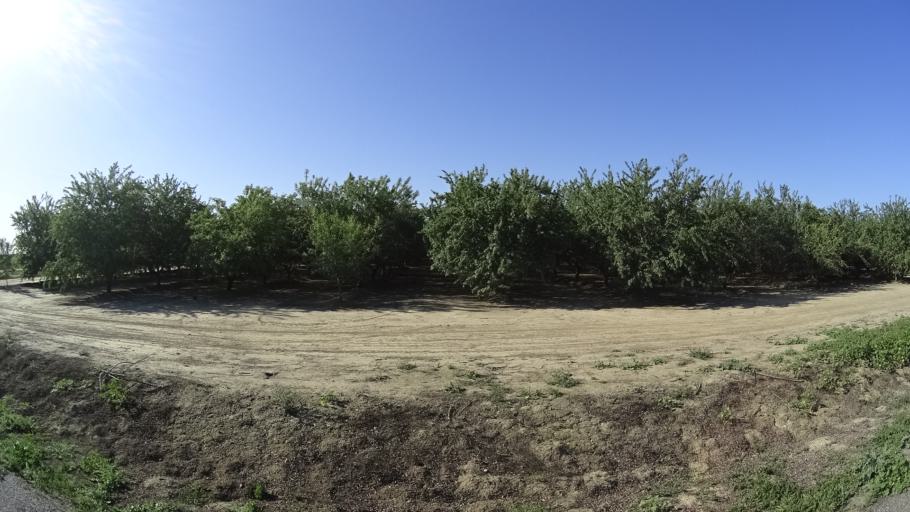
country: US
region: California
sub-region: Glenn County
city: Hamilton City
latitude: 39.6948
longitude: -122.0554
